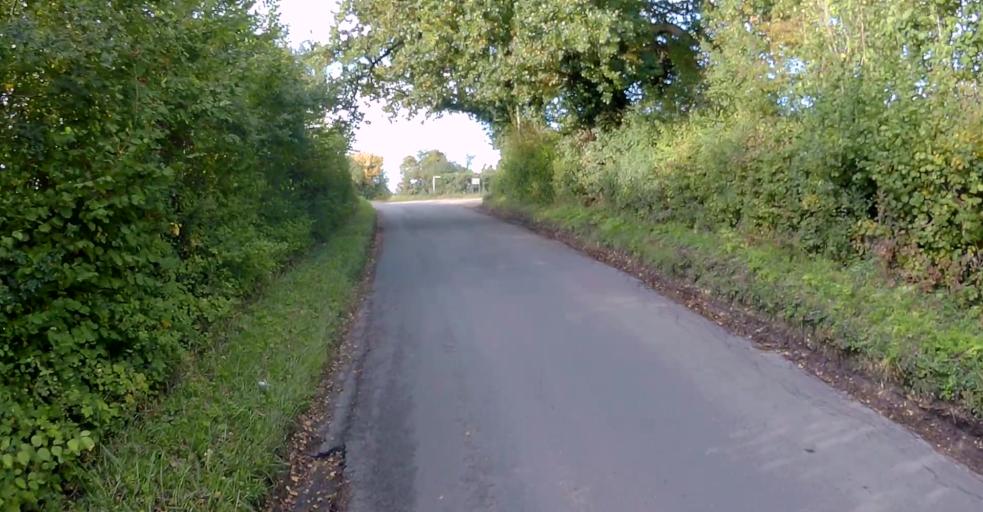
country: GB
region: England
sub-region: Surrey
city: Farnham
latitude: 51.2080
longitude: -0.8284
